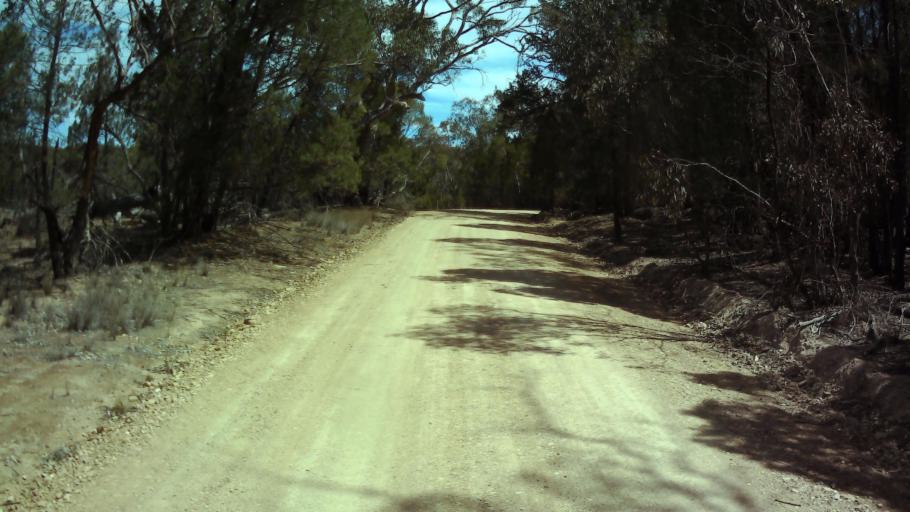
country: AU
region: New South Wales
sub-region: Weddin
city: Grenfell
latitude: -33.8085
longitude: 148.1594
